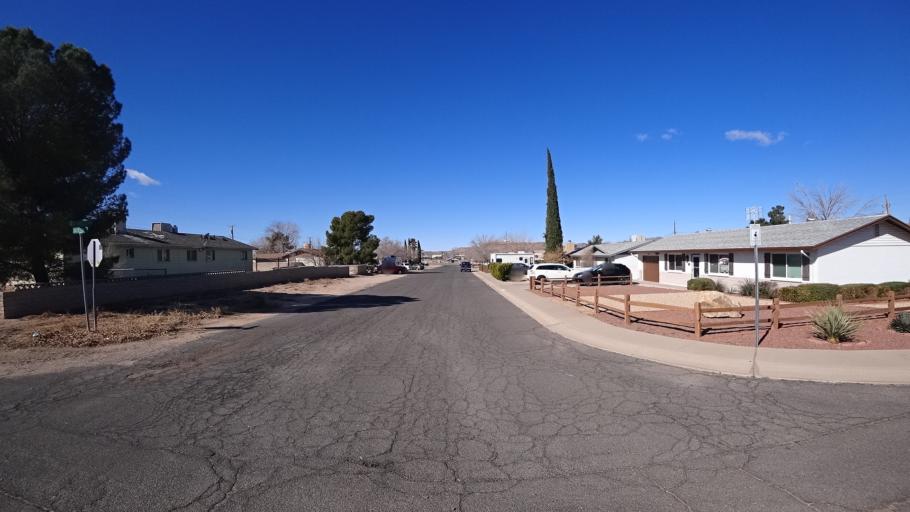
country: US
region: Arizona
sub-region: Mohave County
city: Kingman
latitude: 35.1949
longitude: -114.0202
